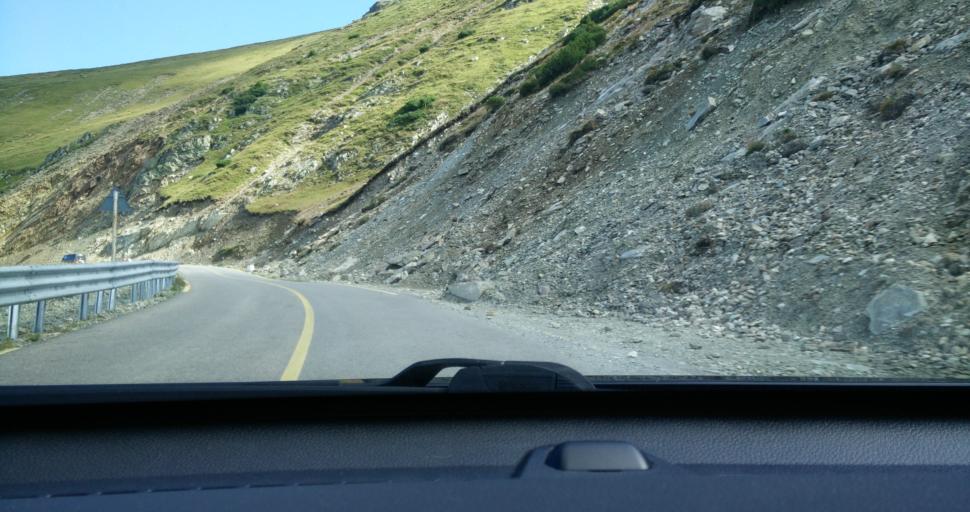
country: RO
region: Gorj
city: Novaci-Straini
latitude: 45.3257
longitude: 23.6824
